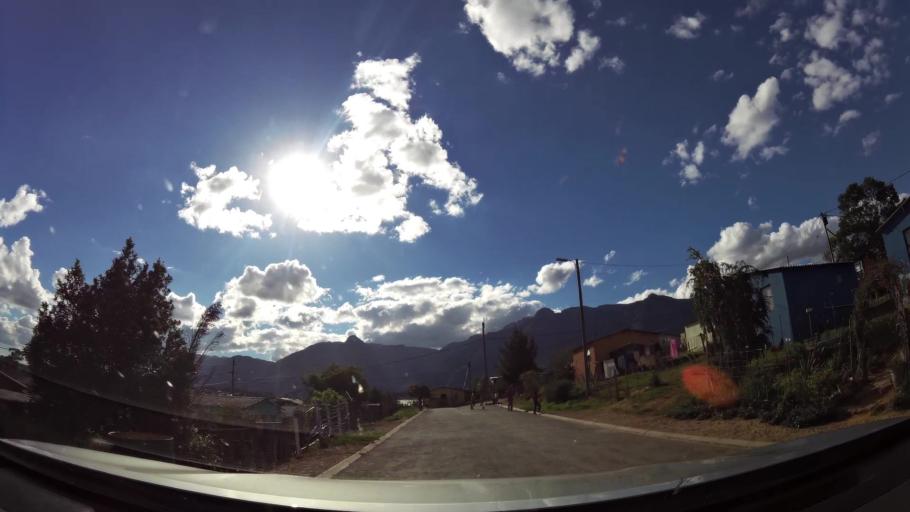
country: ZA
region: Western Cape
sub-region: Overberg District Municipality
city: Swellendam
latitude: -34.0317
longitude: 20.4491
